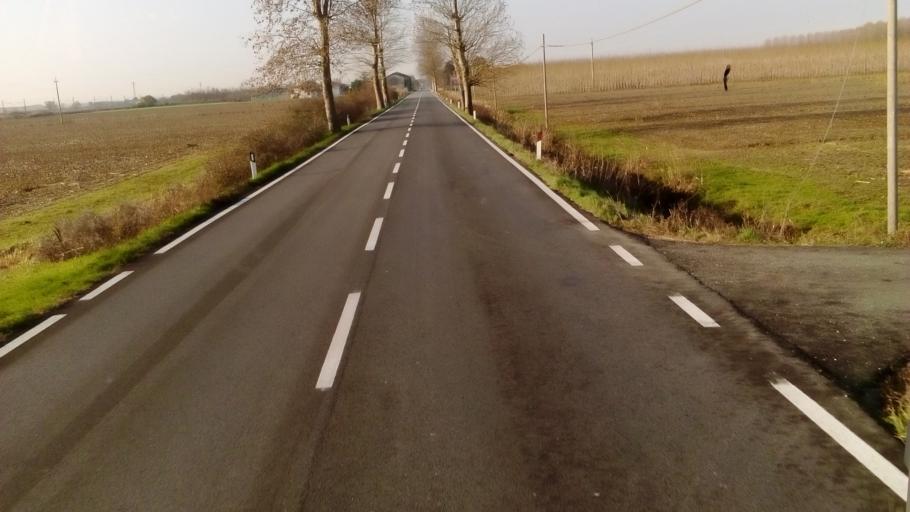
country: IT
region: Friuli Venezia Giulia
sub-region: Provincia di Udine
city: Muzzana del Turgnano
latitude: 45.8243
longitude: 13.1522
